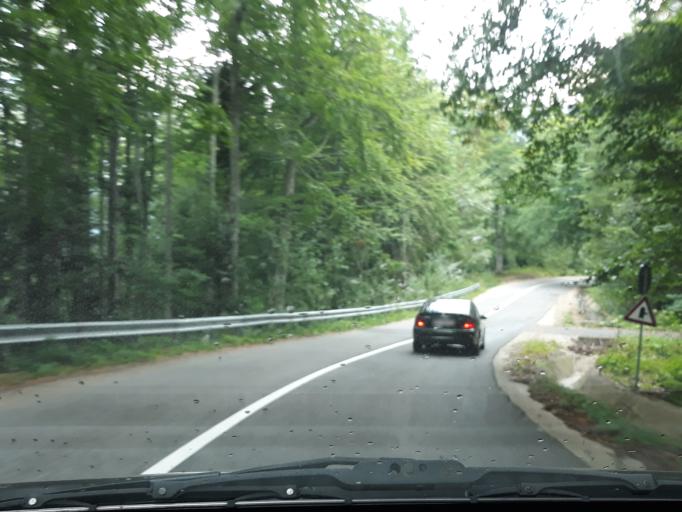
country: RO
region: Bihor
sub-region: Comuna Pietroasa
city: Pietroasa
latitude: 46.5969
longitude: 22.6687
